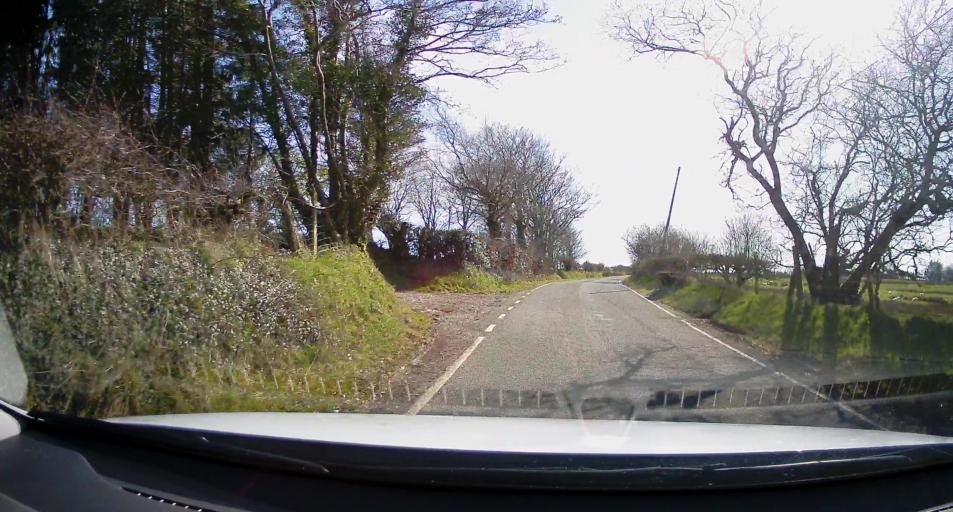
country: GB
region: Wales
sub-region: County of Ceredigion
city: Lledrod
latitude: 52.2907
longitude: -4.0656
